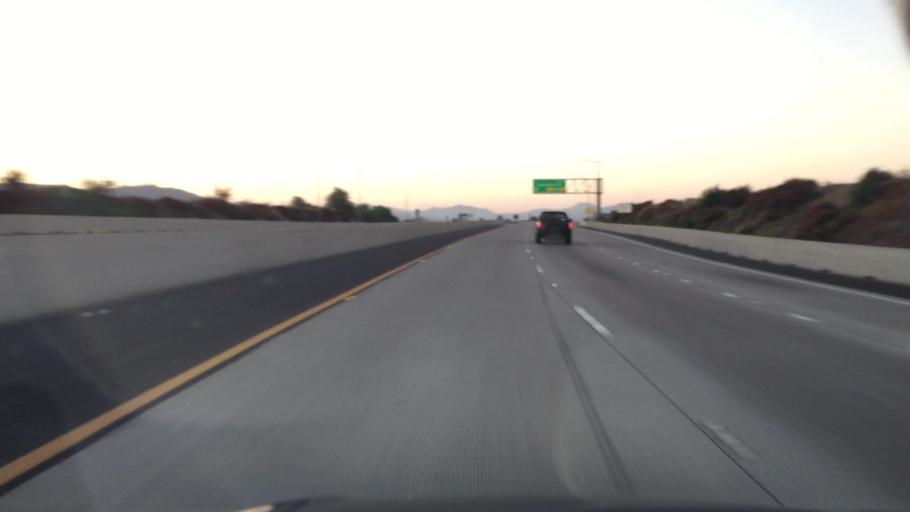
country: US
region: California
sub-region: San Diego County
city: Santee
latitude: 32.8355
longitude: -116.9905
